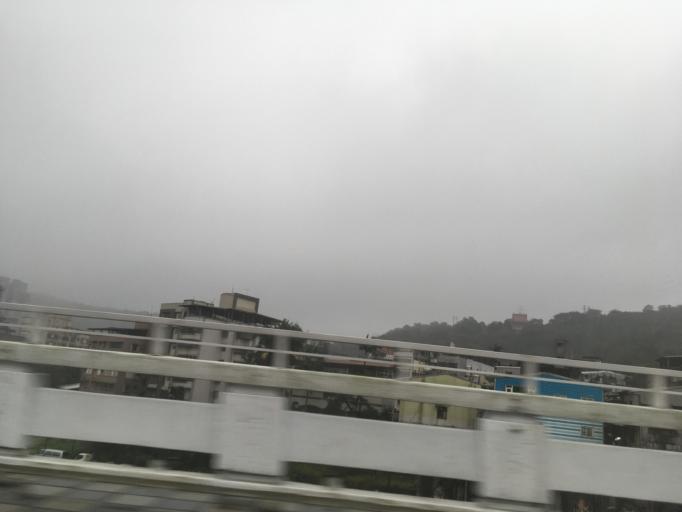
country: TW
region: Taiwan
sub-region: Keelung
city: Keelung
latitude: 25.1016
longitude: 121.7359
